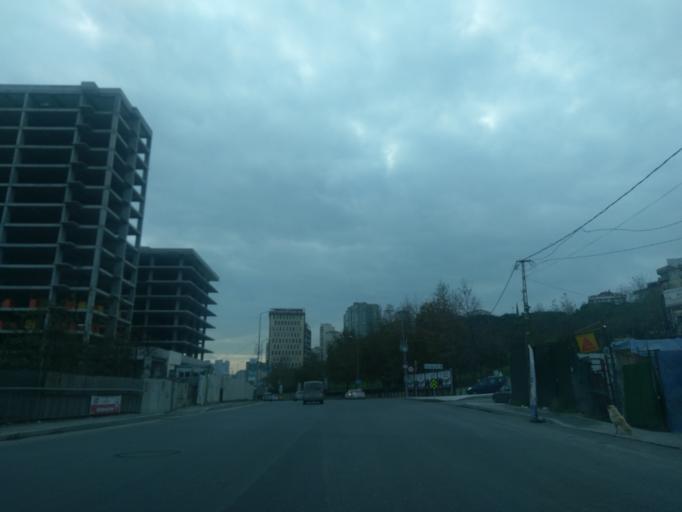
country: TR
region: Istanbul
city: Sisli
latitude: 41.0988
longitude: 28.9781
